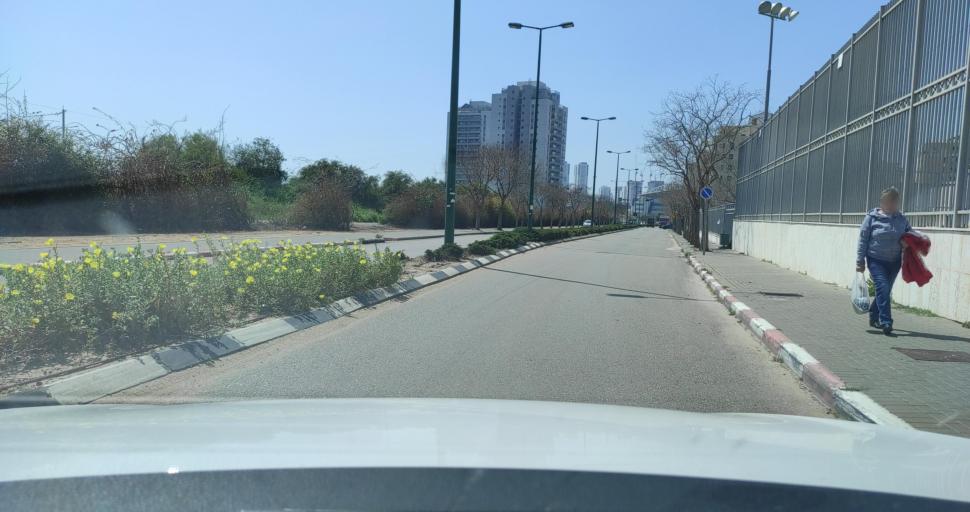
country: IL
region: Central District
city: Even Yehuda
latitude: 32.2953
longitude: 34.8732
